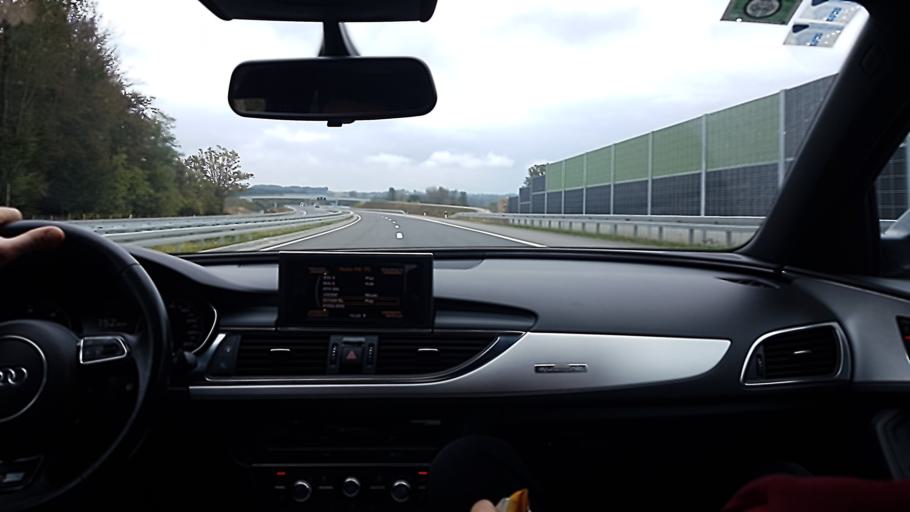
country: BA
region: Republika Srpska
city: Stanari
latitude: 44.8435
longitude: 17.7849
